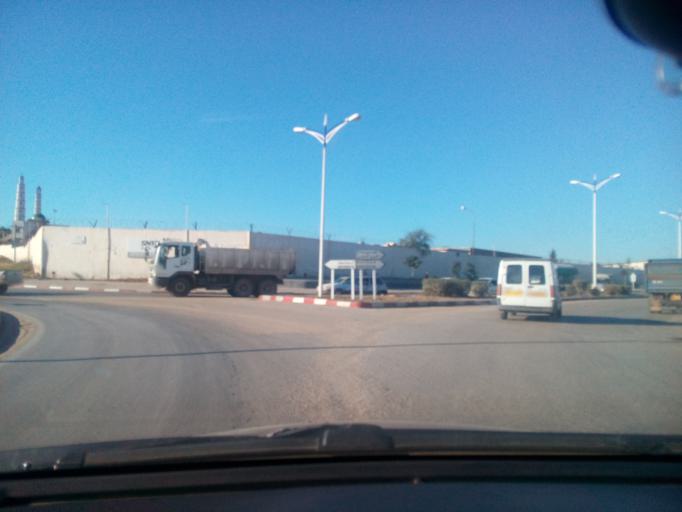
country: DZ
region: Mostaganem
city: Mostaganem
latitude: 35.9232
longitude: 0.1178
